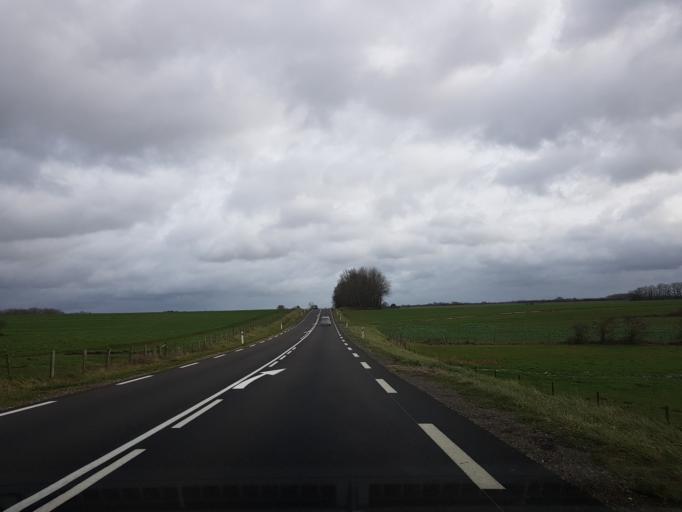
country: FR
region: Champagne-Ardenne
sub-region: Departement de la Haute-Marne
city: Chalindrey
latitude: 47.8491
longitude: 5.4189
